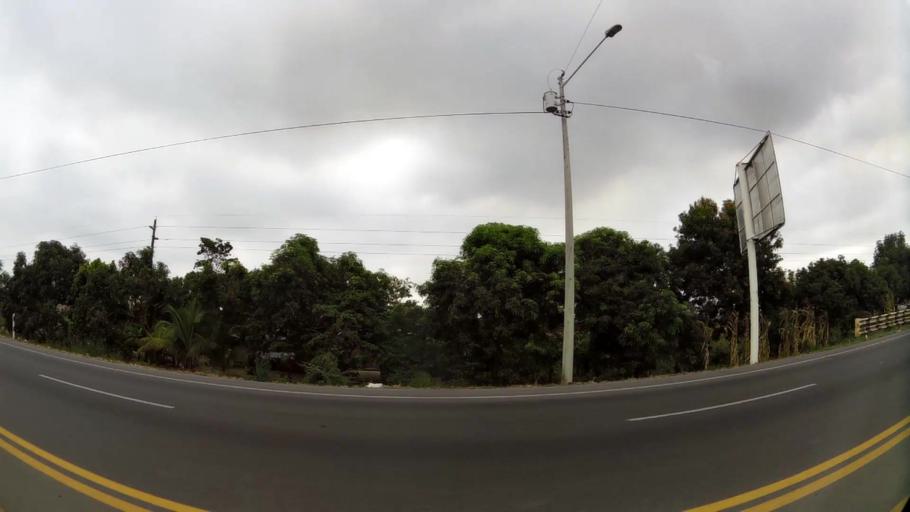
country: EC
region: Guayas
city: Yaguachi Nuevo
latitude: -2.2604
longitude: -79.6368
